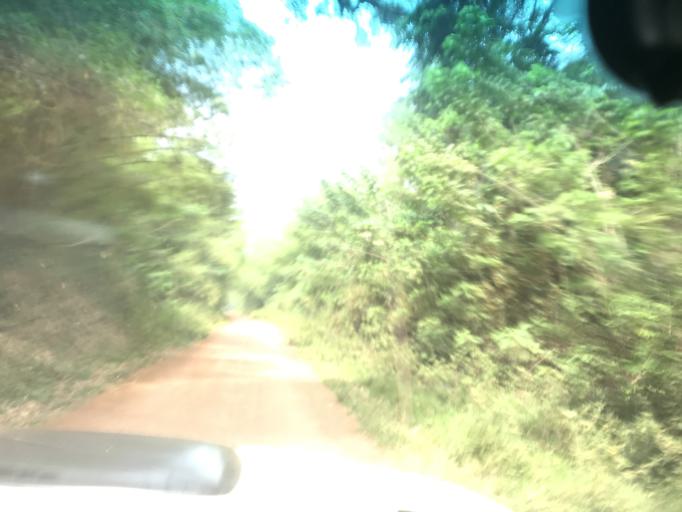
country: CD
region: Eastern Province
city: Buta
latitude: 2.8789
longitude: 24.4688
